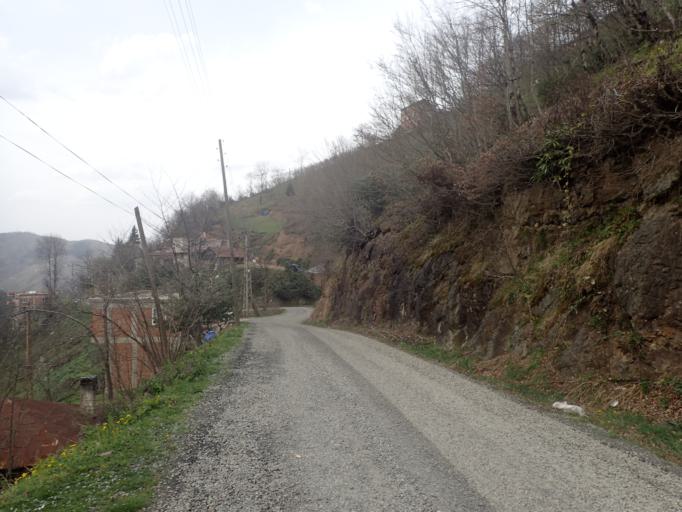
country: TR
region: Ordu
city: Kabaduz
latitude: 40.7762
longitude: 37.9052
